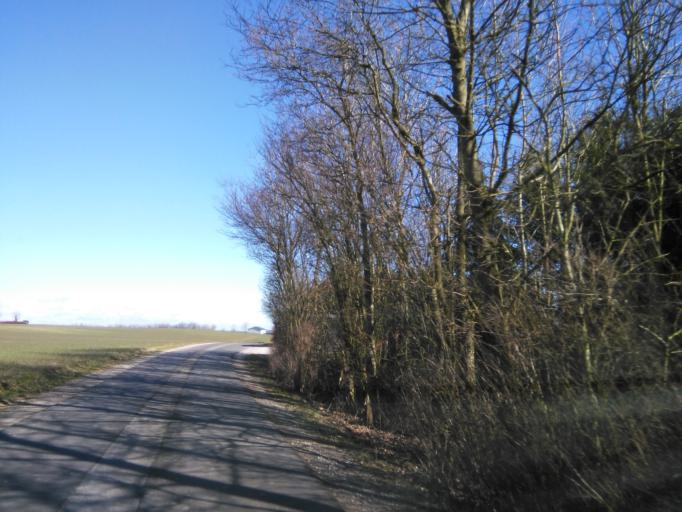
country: DK
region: Central Jutland
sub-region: Skanderborg Kommune
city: Ry
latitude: 56.1370
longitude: 9.7911
